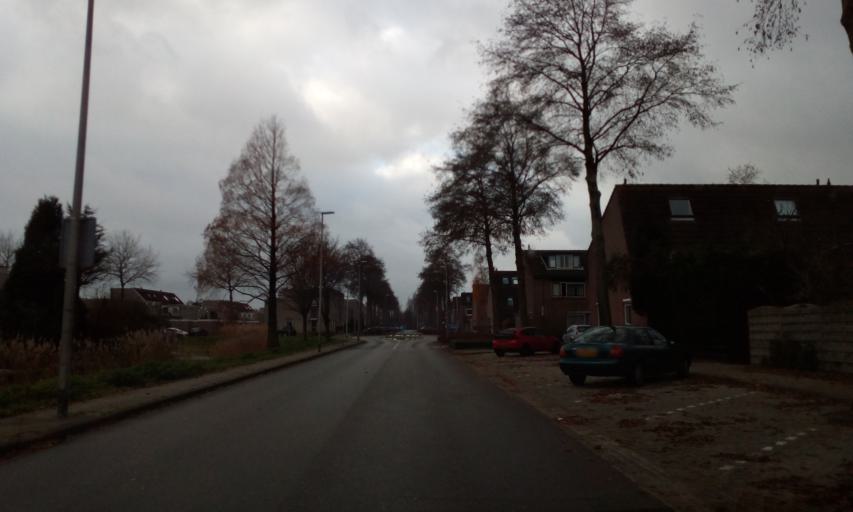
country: NL
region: South Holland
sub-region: Gemeente Zoetermeer
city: Zoetermeer
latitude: 52.0420
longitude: 4.4875
